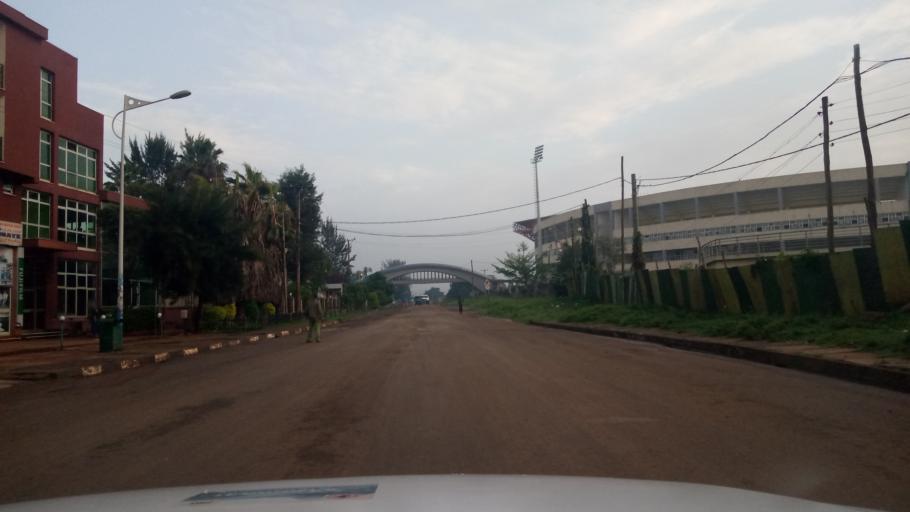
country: ET
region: Oromiya
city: Jima
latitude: 7.6750
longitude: 36.8531
